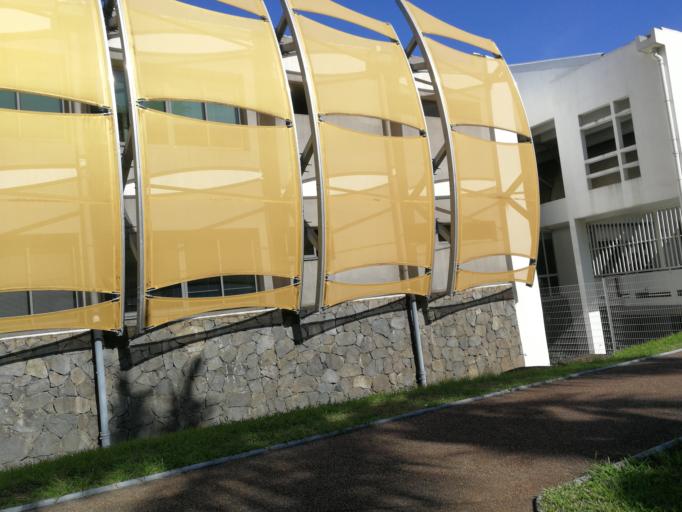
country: RE
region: Reunion
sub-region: Reunion
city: Saint-Denis
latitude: -20.8857
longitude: 55.4669
